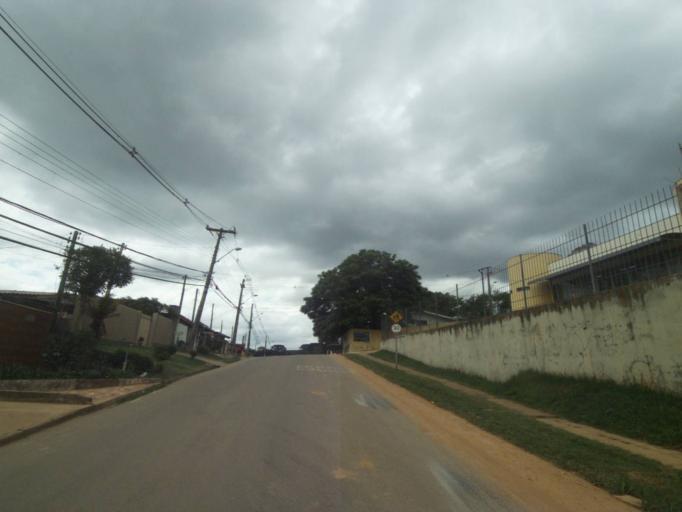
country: BR
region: Parana
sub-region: Curitiba
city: Curitiba
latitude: -25.3895
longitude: -49.2947
